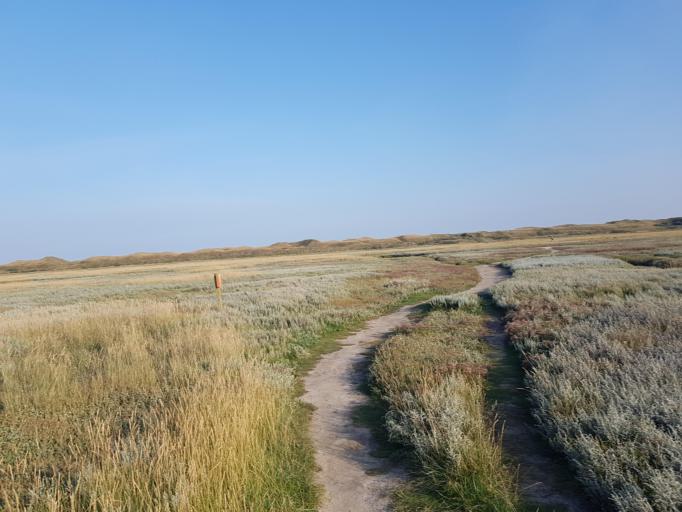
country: NL
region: North Holland
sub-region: Gemeente Texel
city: Den Burg
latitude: 53.1355
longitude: 4.8101
